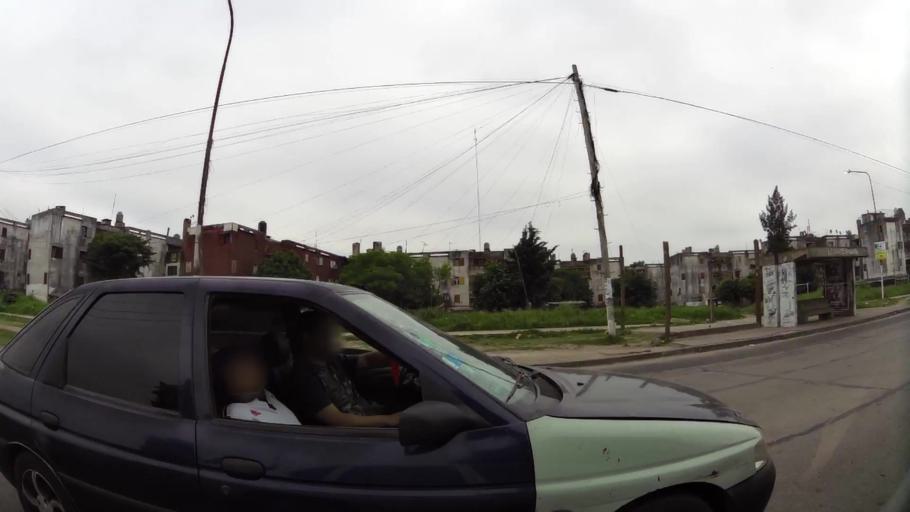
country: AR
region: Buenos Aires
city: San Justo
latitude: -34.7008
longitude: -58.5426
